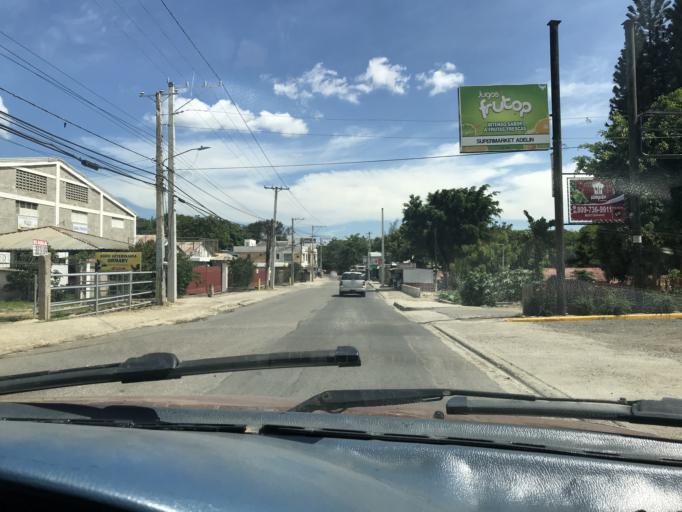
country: DO
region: Santiago
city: Tamboril
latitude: 19.4995
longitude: -70.6521
